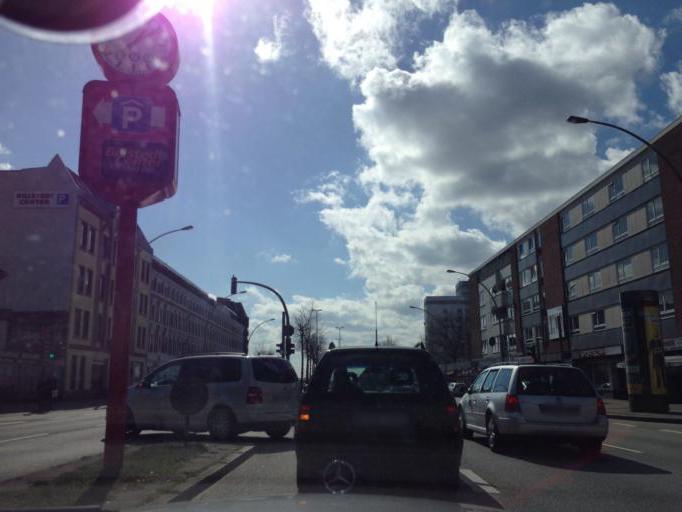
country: DE
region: Hamburg
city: Wandsbek
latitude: 53.5415
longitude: 10.1018
